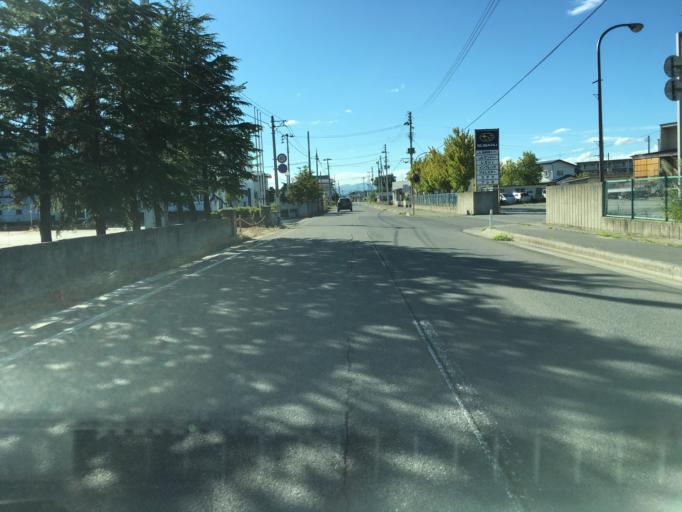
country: JP
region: Yamagata
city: Takahata
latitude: 37.9878
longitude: 140.1487
